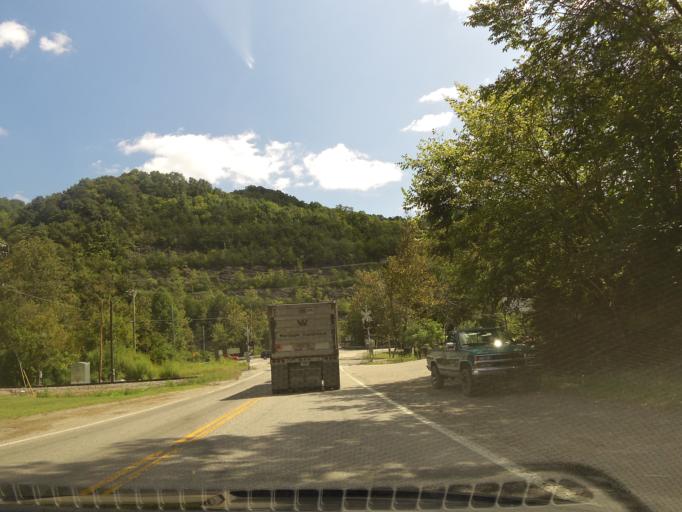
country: US
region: Kentucky
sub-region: Harlan County
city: Harlan
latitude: 36.8681
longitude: -83.3176
